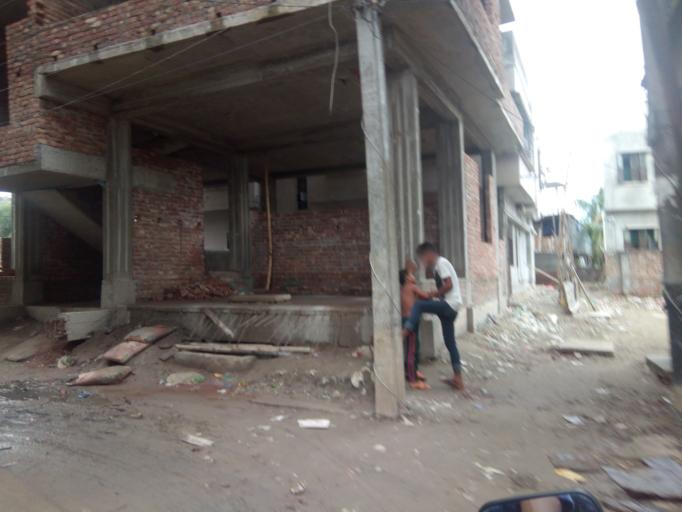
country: BD
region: Dhaka
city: Paltan
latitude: 23.7544
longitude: 90.4349
